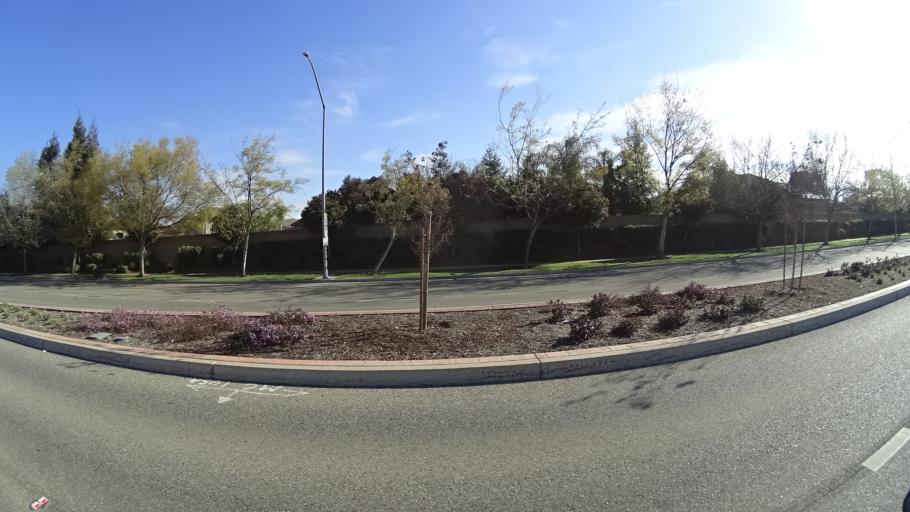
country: US
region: California
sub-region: Fresno County
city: Biola
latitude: 36.8323
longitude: -119.9071
